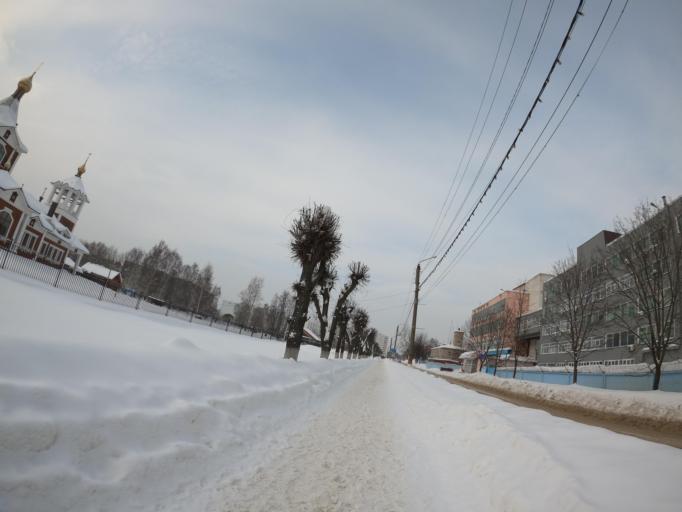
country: RU
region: Moskovskaya
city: Elektrogorsk
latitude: 55.8855
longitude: 38.7818
